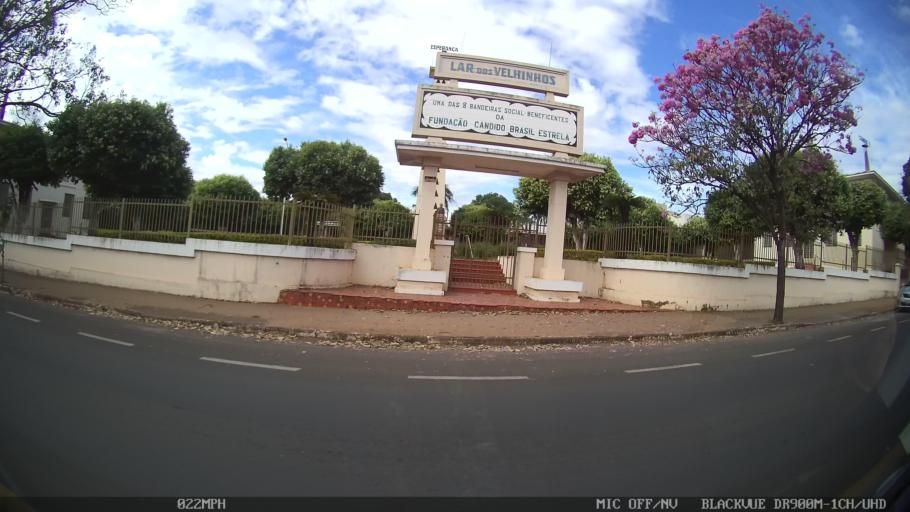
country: BR
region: Sao Paulo
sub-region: Bady Bassitt
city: Bady Bassitt
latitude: -20.8113
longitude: -49.5092
